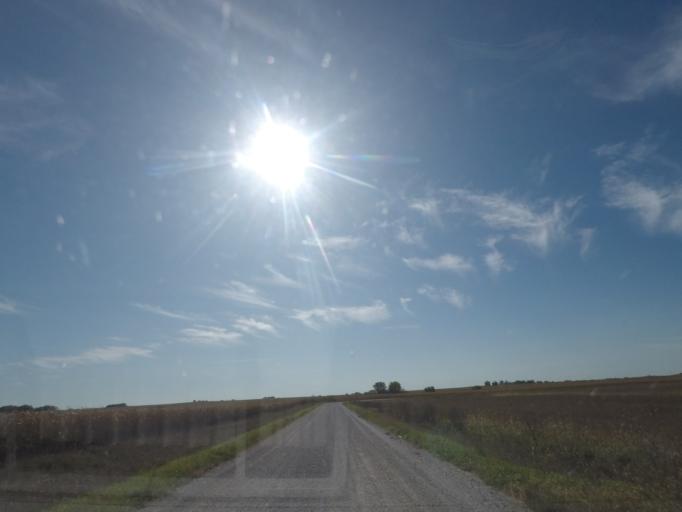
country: US
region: Iowa
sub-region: Story County
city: Nevada
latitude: 42.0008
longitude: -93.3189
